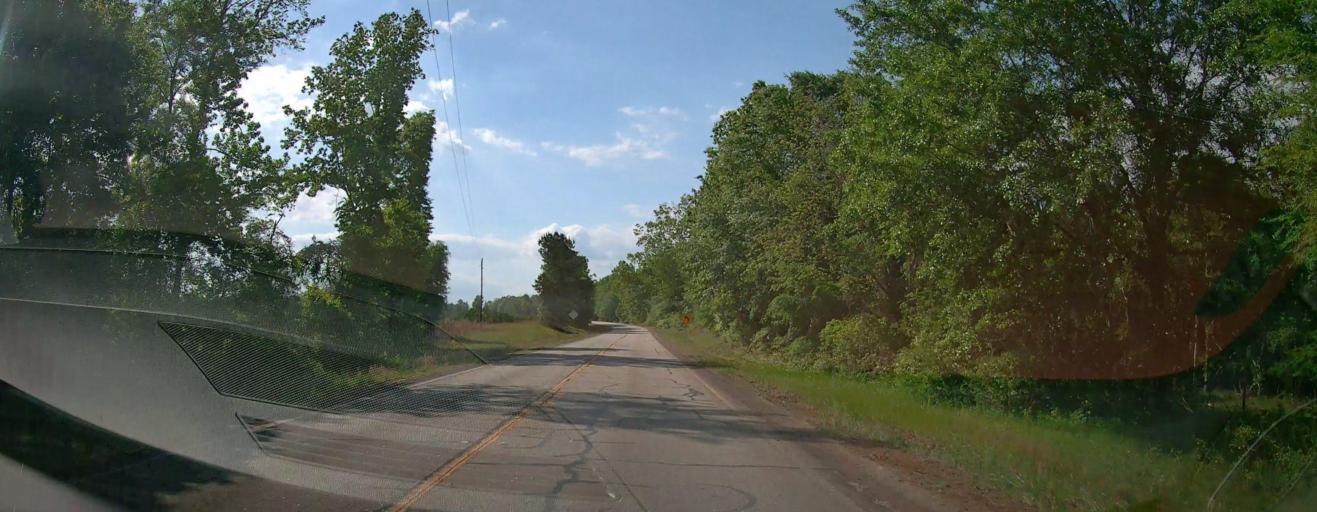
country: US
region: Georgia
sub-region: Washington County
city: Tennille
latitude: 32.9064
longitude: -82.9726
